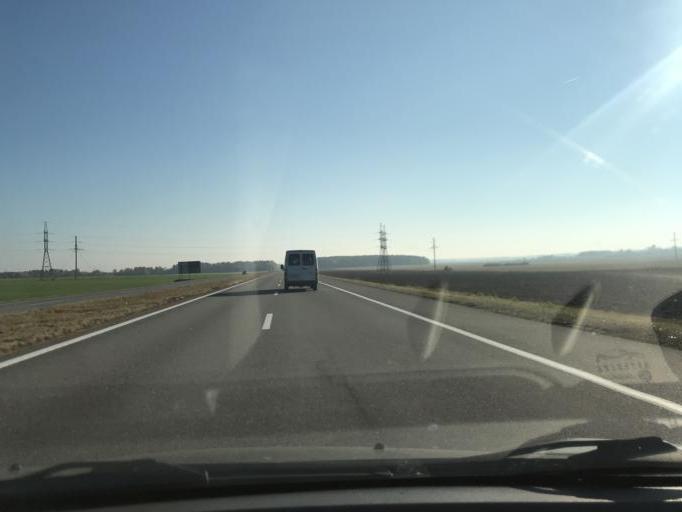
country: BY
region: Minsk
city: Blon'
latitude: 53.5458
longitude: 28.1842
